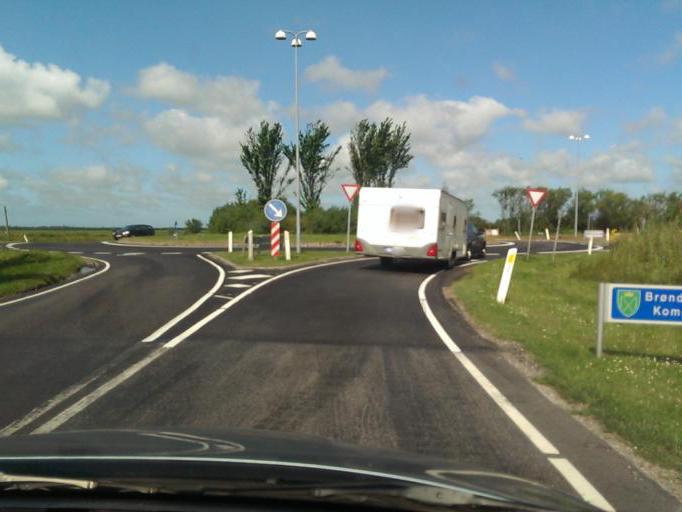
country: DK
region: North Denmark
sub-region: Alborg Kommune
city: Vadum
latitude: 57.2166
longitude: 9.8384
